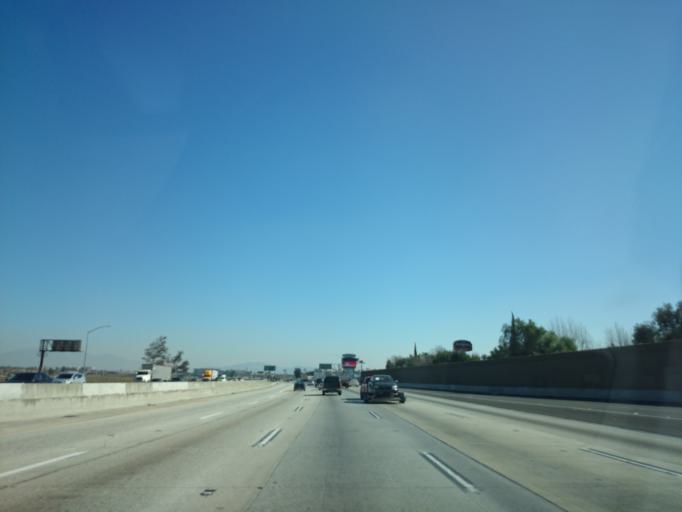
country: US
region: California
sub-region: San Bernardino County
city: Rancho Cucamonga
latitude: 34.0693
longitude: -117.6081
